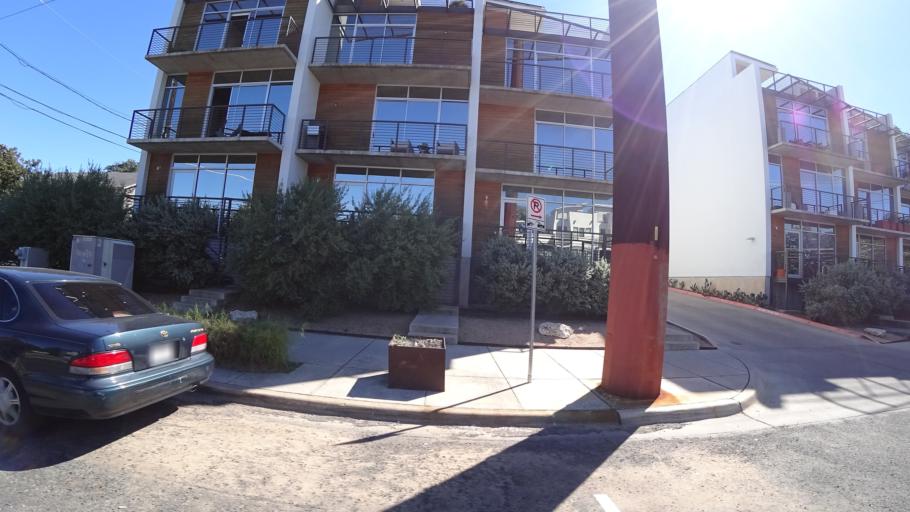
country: US
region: Texas
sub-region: Travis County
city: Austin
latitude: 30.2449
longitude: -97.7642
